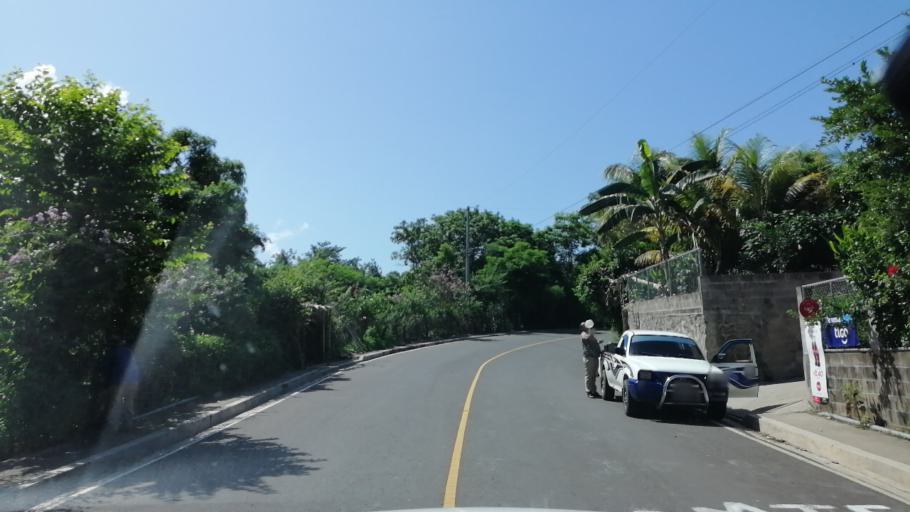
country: SV
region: Cabanas
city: Victoria
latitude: 13.9505
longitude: -88.7299
